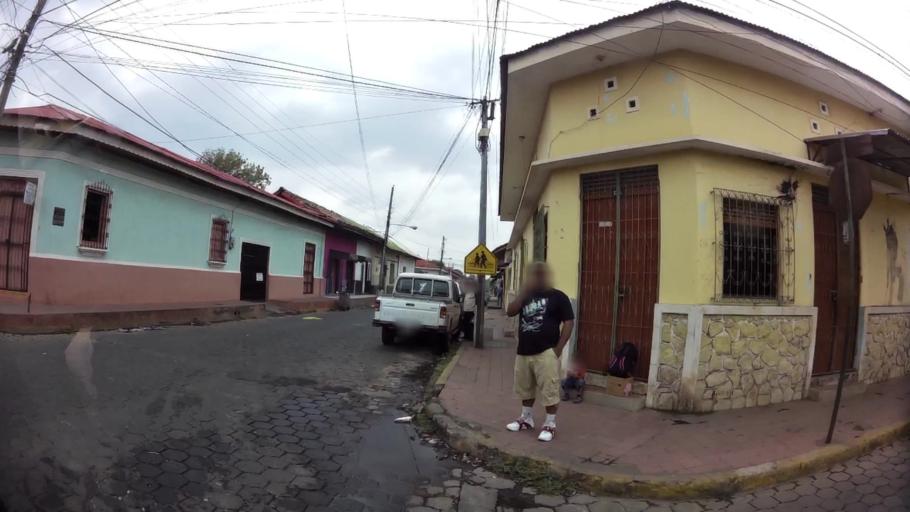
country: NI
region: Leon
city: Leon
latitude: 12.4342
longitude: -86.8757
